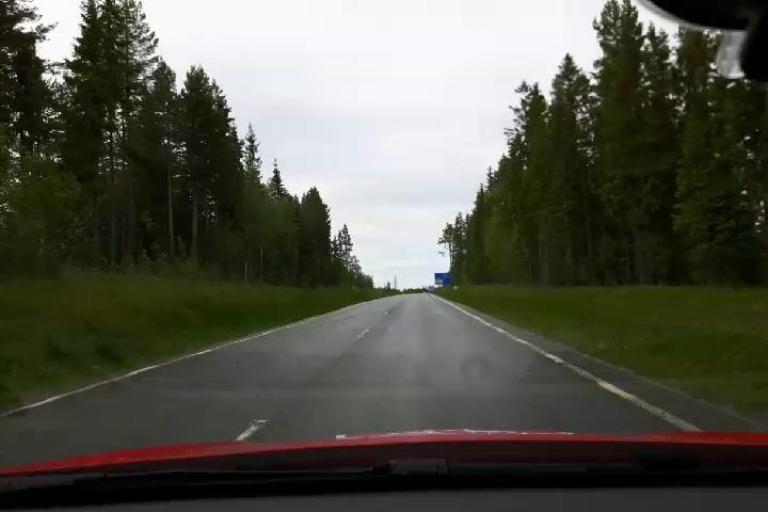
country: SE
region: Jaemtland
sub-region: Bergs Kommun
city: Hoverberg
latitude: 62.9124
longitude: 14.3294
